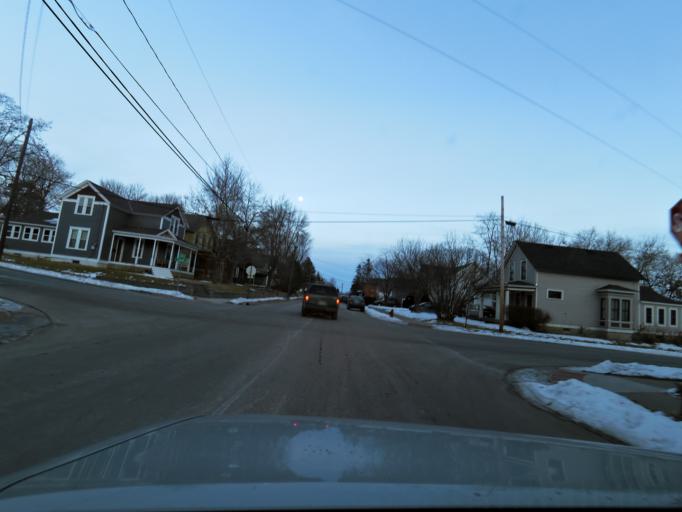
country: US
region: Minnesota
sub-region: Washington County
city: Stillwater
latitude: 45.0602
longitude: -92.8168
